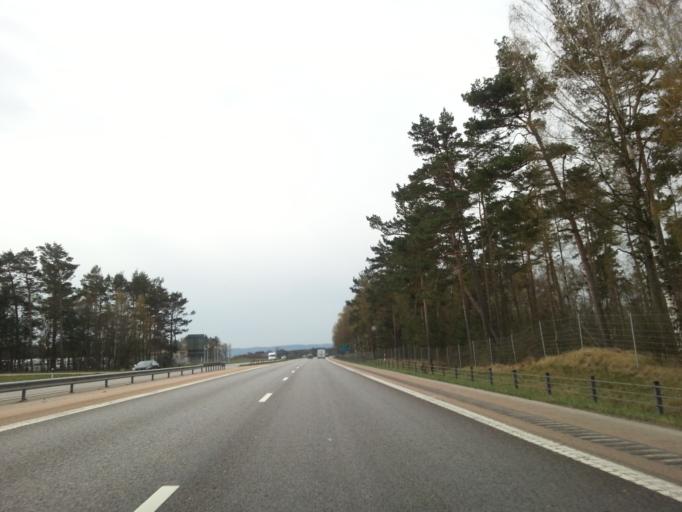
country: SE
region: Halland
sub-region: Laholms Kommun
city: Mellbystrand
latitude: 56.4979
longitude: 12.9572
